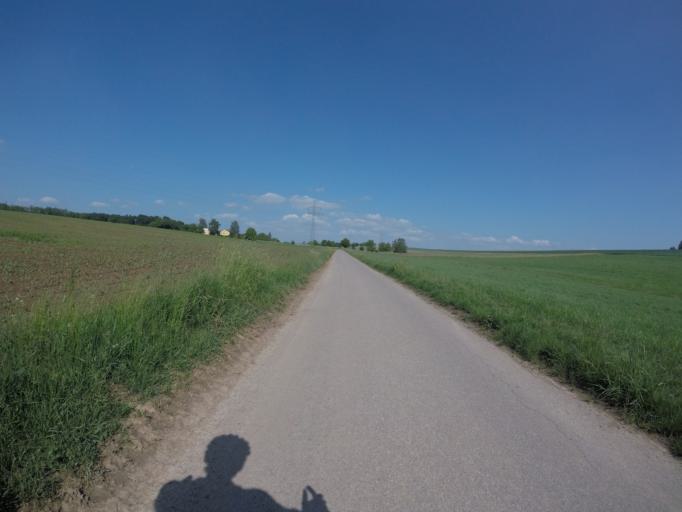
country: DE
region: Baden-Wuerttemberg
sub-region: Regierungsbezirk Stuttgart
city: Kirchberg an der Murr
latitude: 48.9621
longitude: 9.3478
